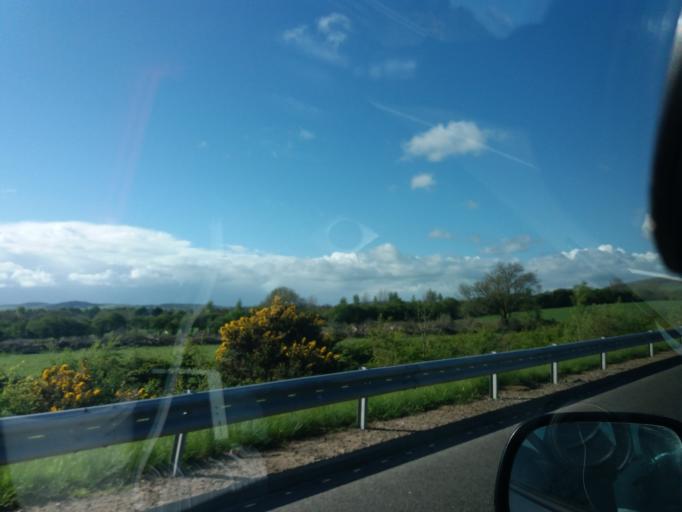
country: IE
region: Munster
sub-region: Waterford
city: Waterford
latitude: 52.3034
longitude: -7.1441
